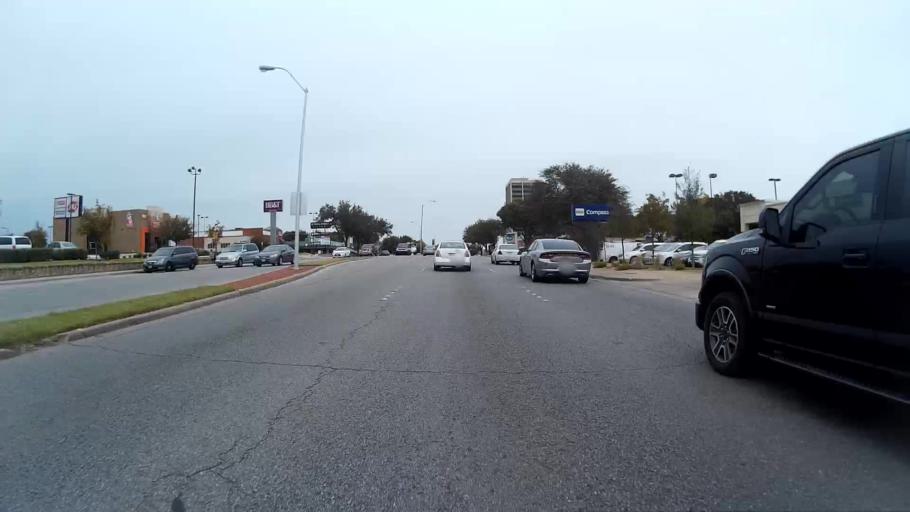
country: US
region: Texas
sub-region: Dallas County
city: Richardson
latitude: 32.9516
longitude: -96.7689
